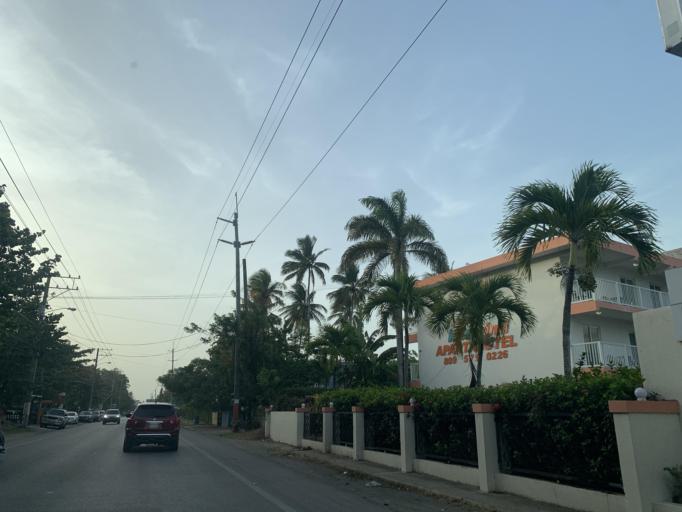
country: DO
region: Puerto Plata
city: Cabarete
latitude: 19.7538
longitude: -70.4171
